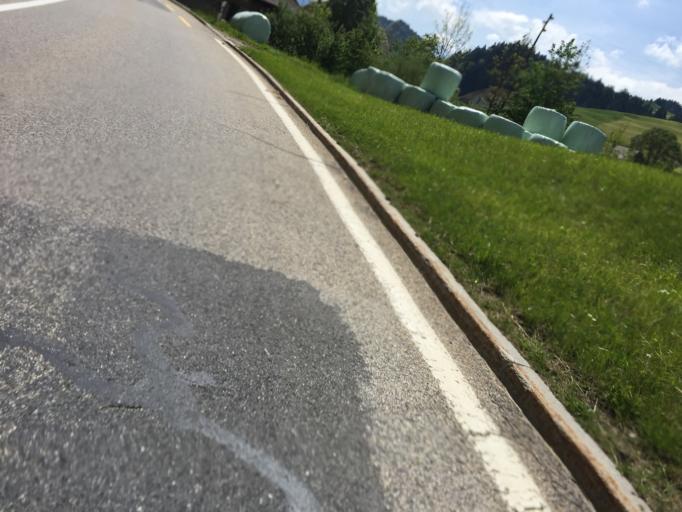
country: CH
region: Bern
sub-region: Emmental District
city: Trub
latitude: 46.9116
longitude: 7.8773
